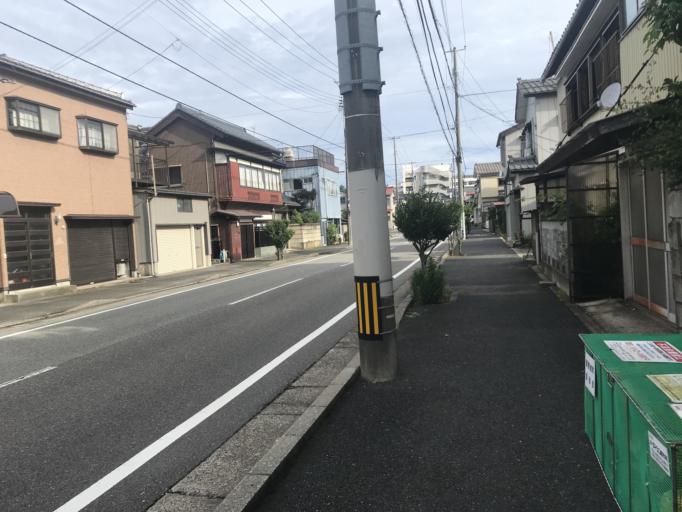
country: JP
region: Niigata
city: Niigata-shi
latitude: 37.9329
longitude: 139.0503
